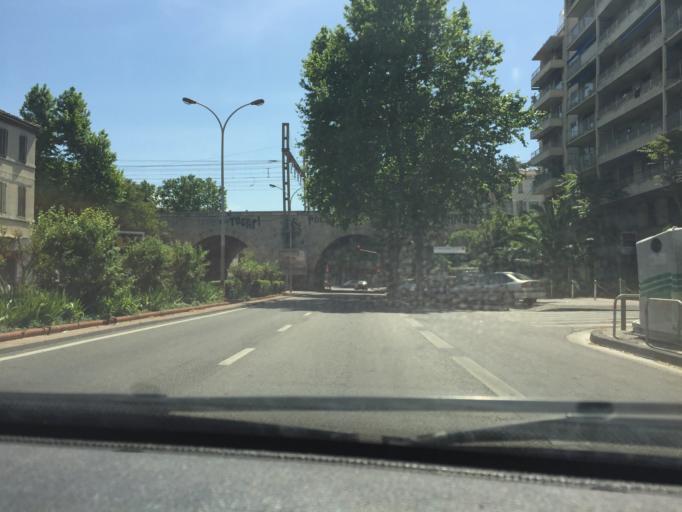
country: FR
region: Provence-Alpes-Cote d'Azur
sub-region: Departement des Bouches-du-Rhone
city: Marseille 04
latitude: 43.3078
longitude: 5.4017
